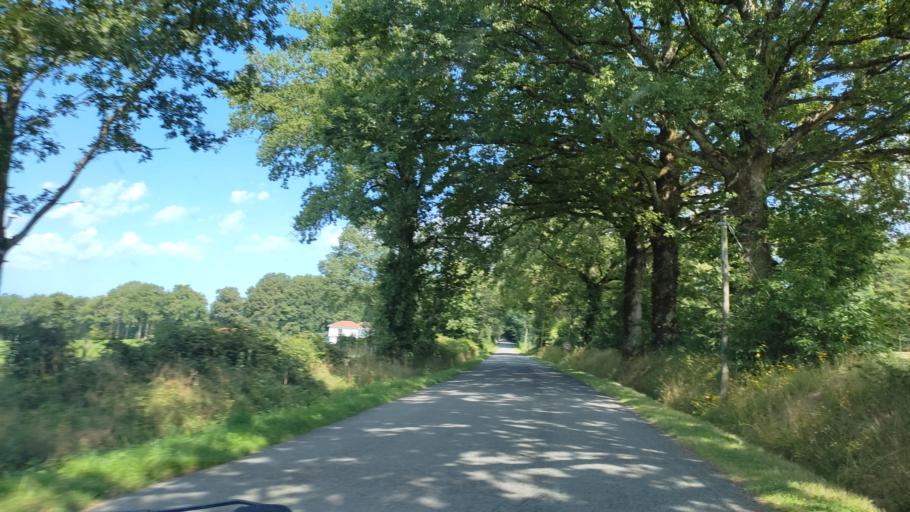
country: FR
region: Limousin
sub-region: Departement de la Haute-Vienne
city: Couzeix
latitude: 45.8514
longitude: 1.1922
